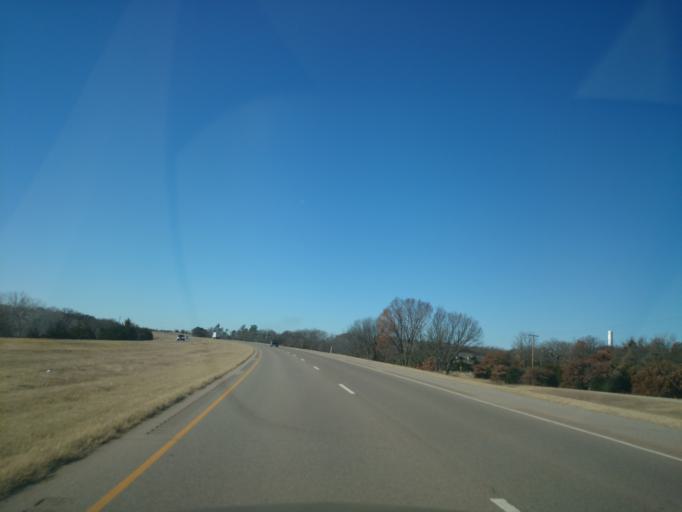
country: US
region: Oklahoma
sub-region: Payne County
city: Stillwater
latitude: 36.1162
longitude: -97.1853
